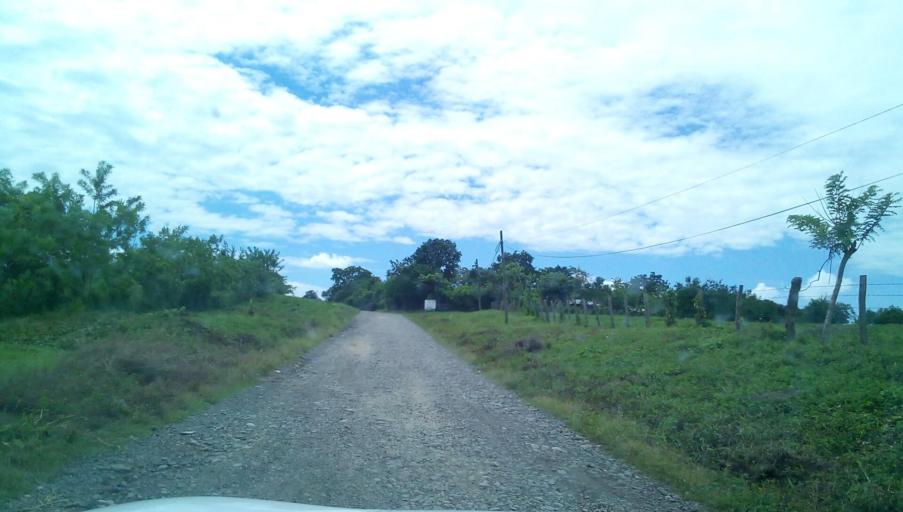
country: MX
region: Veracruz
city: Tepetzintla
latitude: 21.1519
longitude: -97.8552
